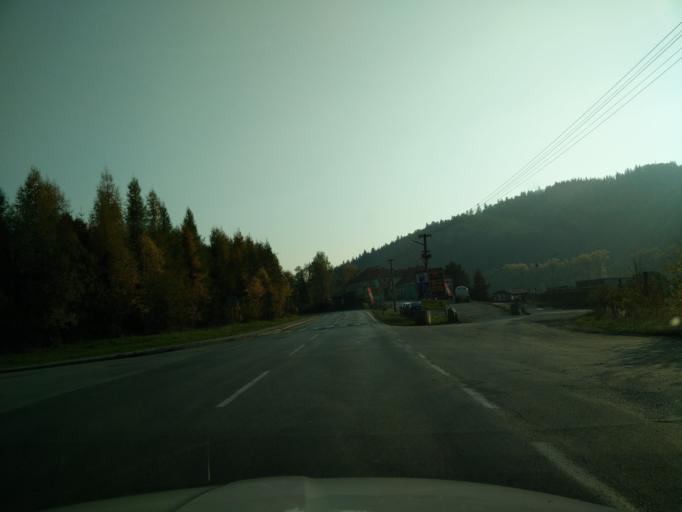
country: SK
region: Zilinsky
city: Cadca
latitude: 49.4190
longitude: 18.8368
